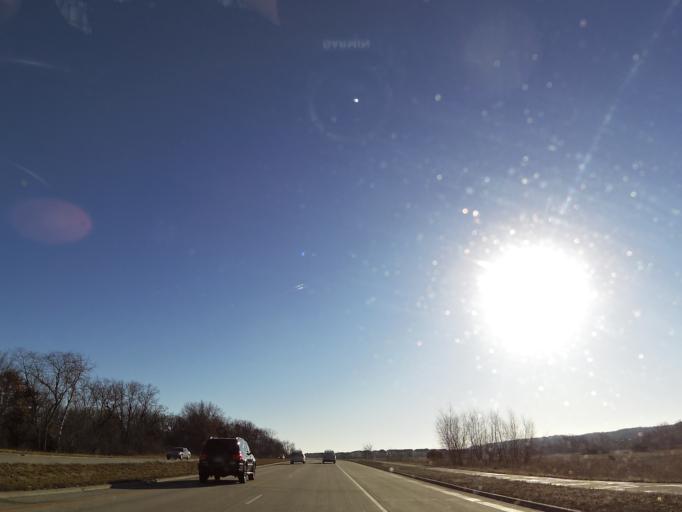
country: US
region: Minnesota
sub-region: Scott County
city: Prior Lake
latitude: 44.7722
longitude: -93.4296
